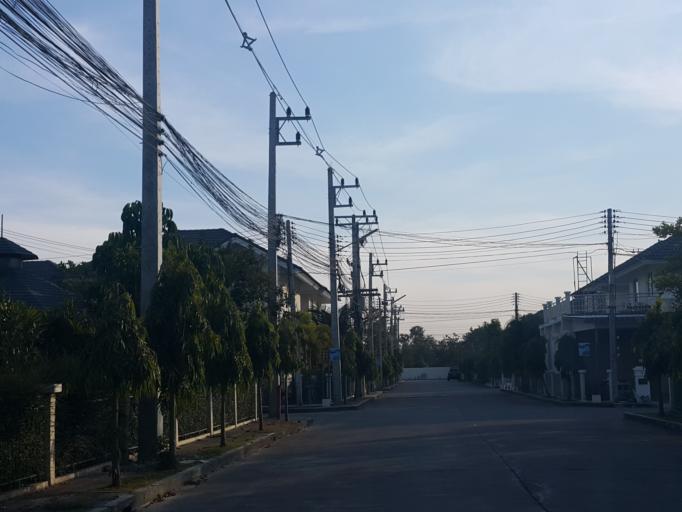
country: TH
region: Chiang Mai
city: San Sai
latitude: 18.8120
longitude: 99.0768
